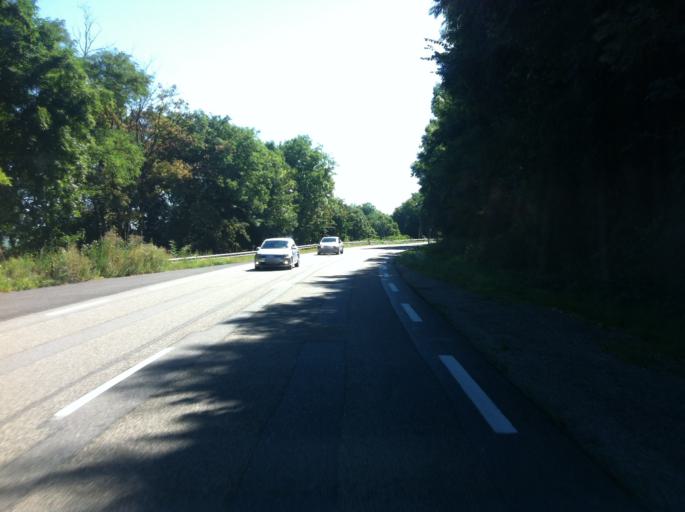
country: FR
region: Alsace
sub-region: Departement du Haut-Rhin
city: Kaysersberg
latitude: 48.1344
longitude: 7.2719
